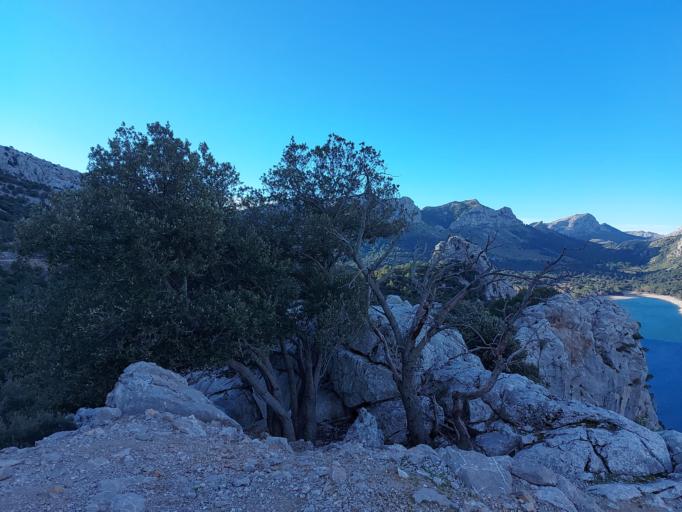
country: ES
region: Balearic Islands
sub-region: Illes Balears
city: Escorca
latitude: 39.8113
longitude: 2.8279
